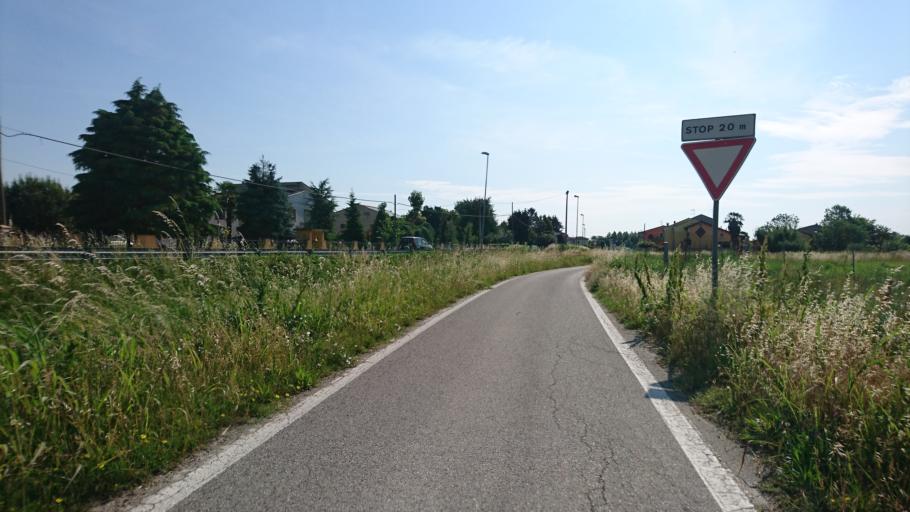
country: IT
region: Veneto
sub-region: Provincia di Padova
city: Merlara
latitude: 45.1736
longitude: 11.4205
